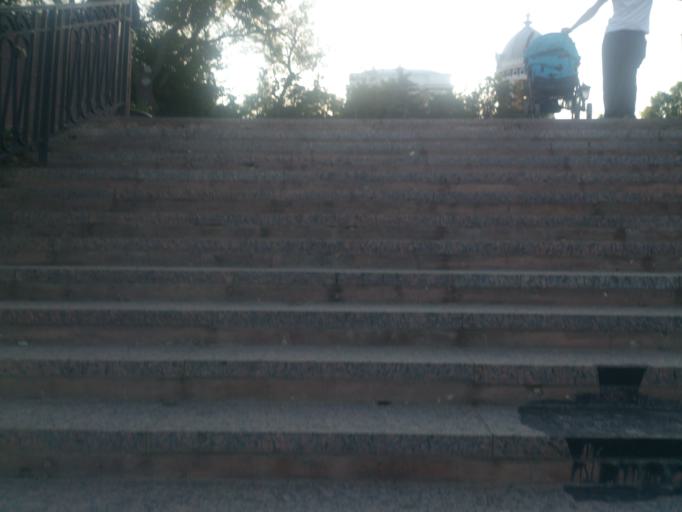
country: RU
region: Ulyanovsk
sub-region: Ulyanovskiy Rayon
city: Ulyanovsk
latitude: 54.3150
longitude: 48.4068
